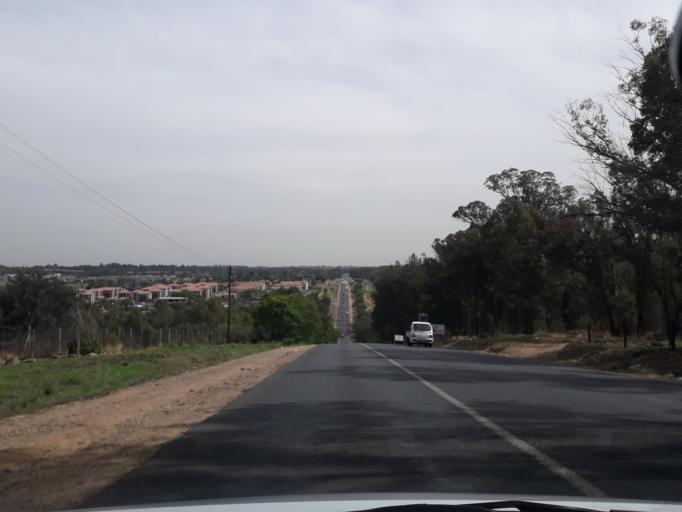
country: ZA
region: Gauteng
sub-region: City of Johannesburg Metropolitan Municipality
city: Diepsloot
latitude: -26.0058
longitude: 28.0397
